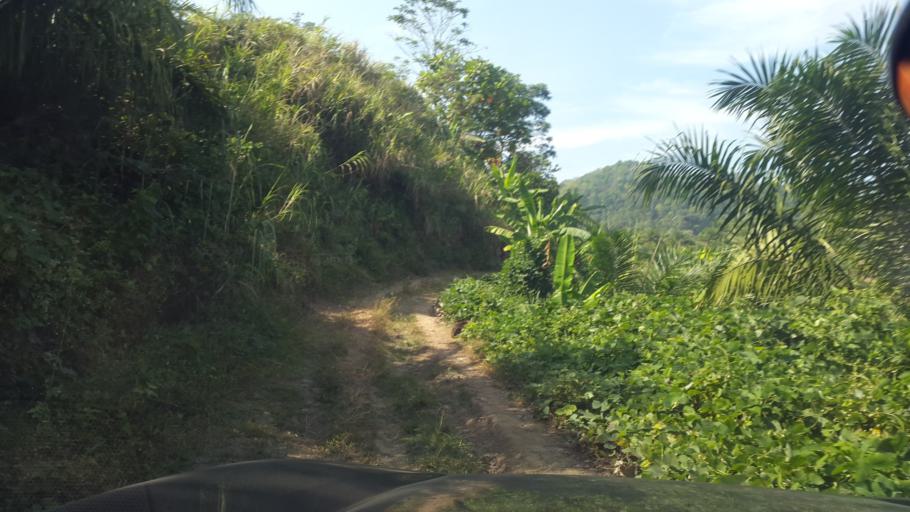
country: ID
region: West Java
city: Bojonggaling
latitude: -6.9280
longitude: 106.6318
